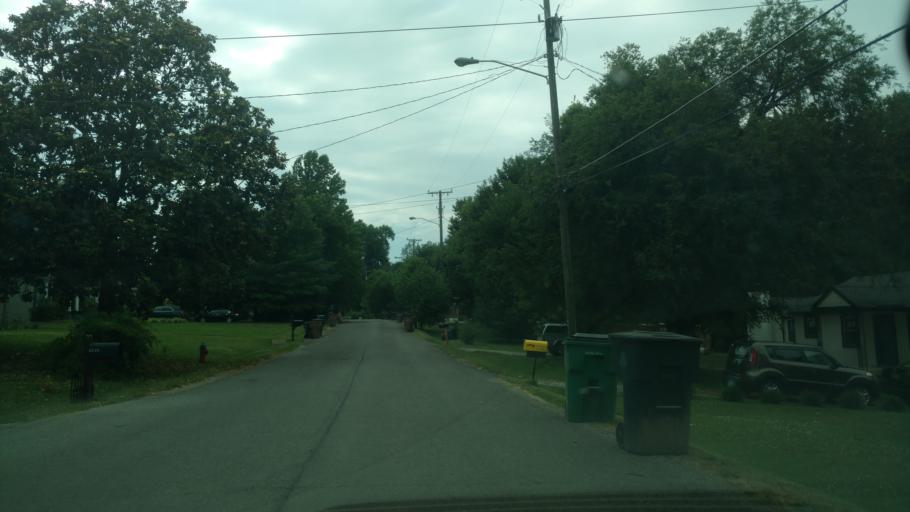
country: US
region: Tennessee
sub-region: Davidson County
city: Lakewood
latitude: 36.2073
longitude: -86.7062
